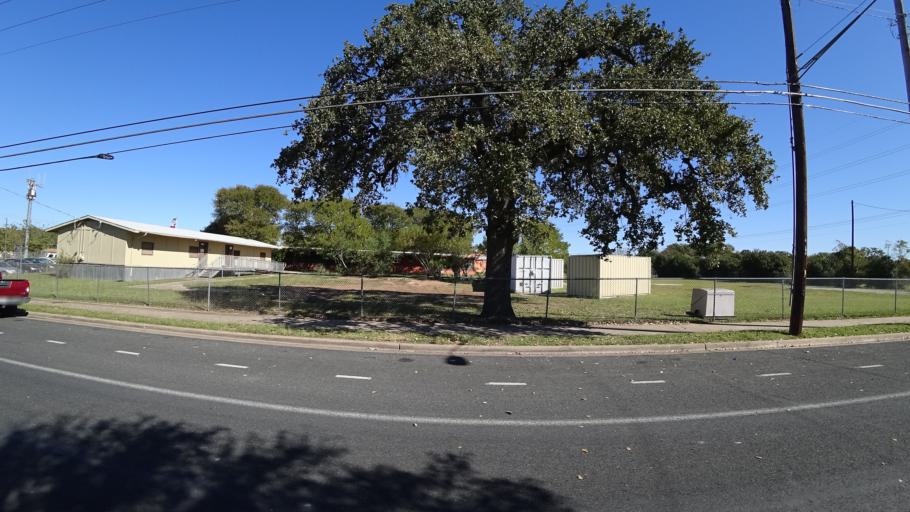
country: US
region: Texas
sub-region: Travis County
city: Austin
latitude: 30.2786
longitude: -97.6861
